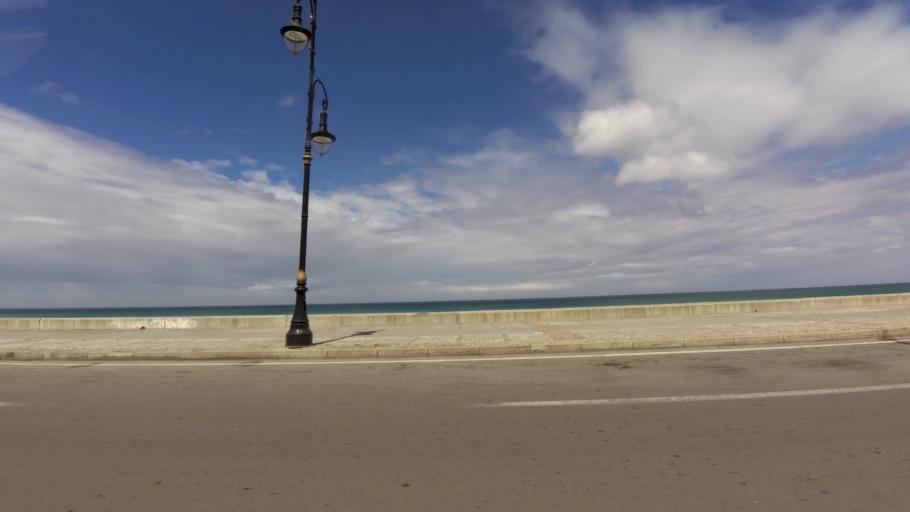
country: MA
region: Tanger-Tetouan
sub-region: Tanger-Assilah
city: Tangier
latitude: 35.7920
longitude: -5.8200
